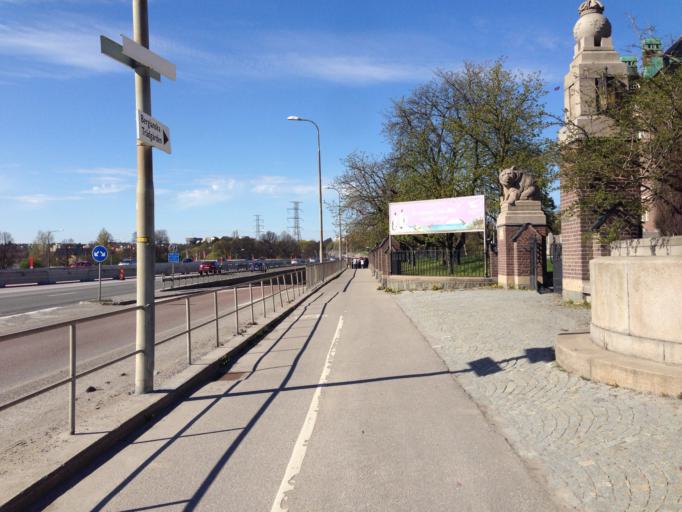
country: SE
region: Stockholm
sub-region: Norrtalje Kommun
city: Bergshamra
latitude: 59.3685
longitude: 18.0521
